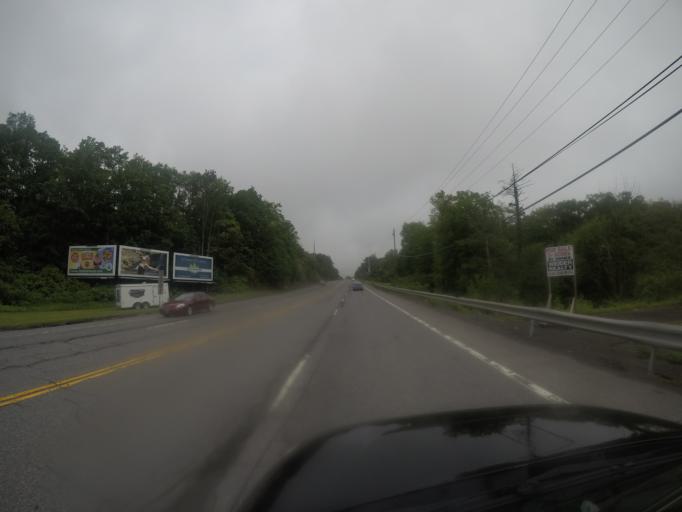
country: US
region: New York
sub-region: Ulster County
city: West Hurley
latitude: 41.9843
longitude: -74.0861
